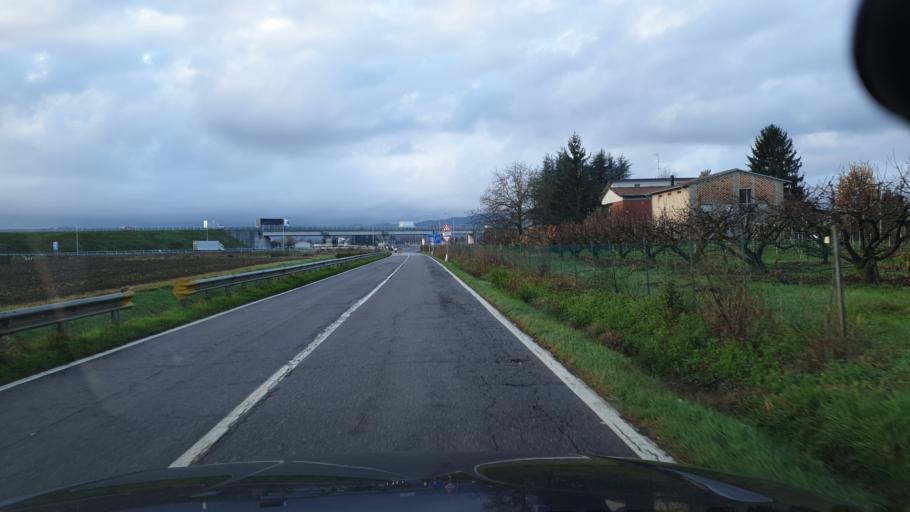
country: IT
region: Emilia-Romagna
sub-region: Provincia di Bologna
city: Crespellano
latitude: 44.5188
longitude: 11.1153
